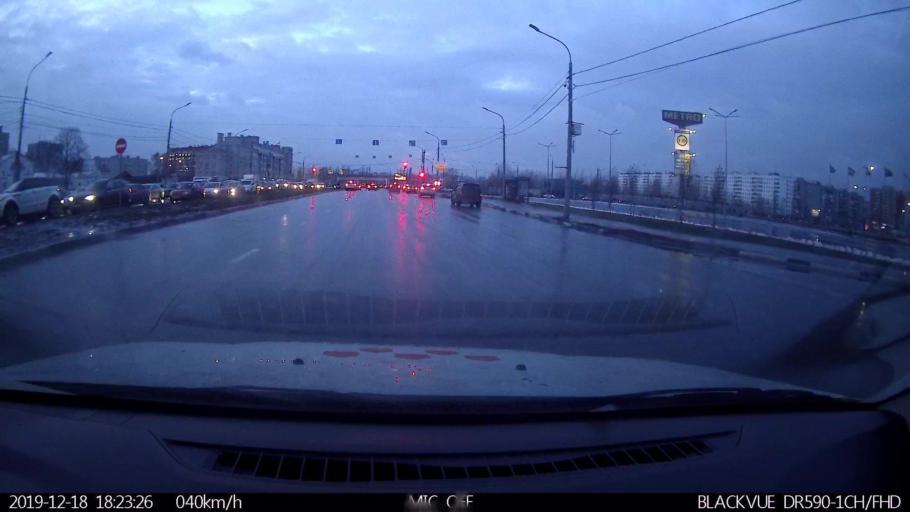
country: RU
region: Nizjnij Novgorod
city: Nizhniy Novgorod
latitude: 56.3328
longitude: 43.9529
